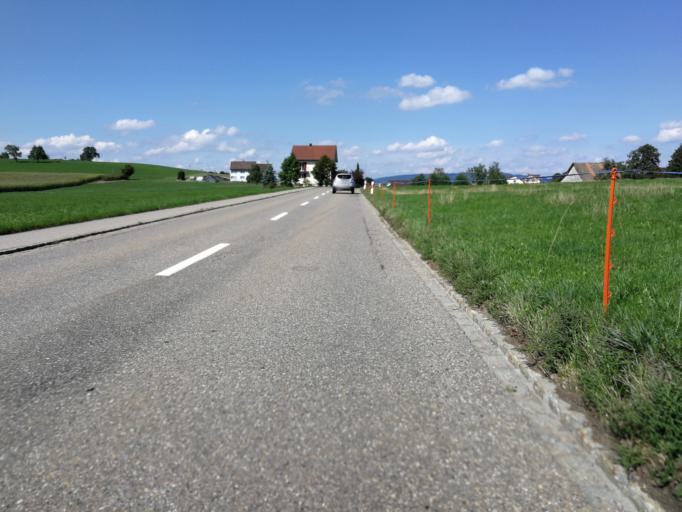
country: CH
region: Zurich
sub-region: Bezirk Horgen
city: Waedenswil / Eichweid
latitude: 47.2113
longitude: 8.6643
